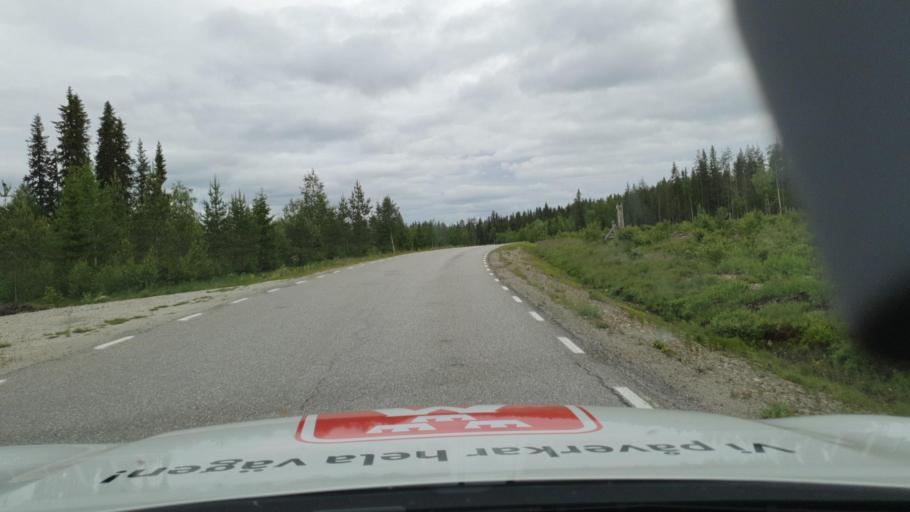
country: SE
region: Vaesterbotten
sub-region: Lycksele Kommun
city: Soderfors
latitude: 64.3014
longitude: 18.1731
